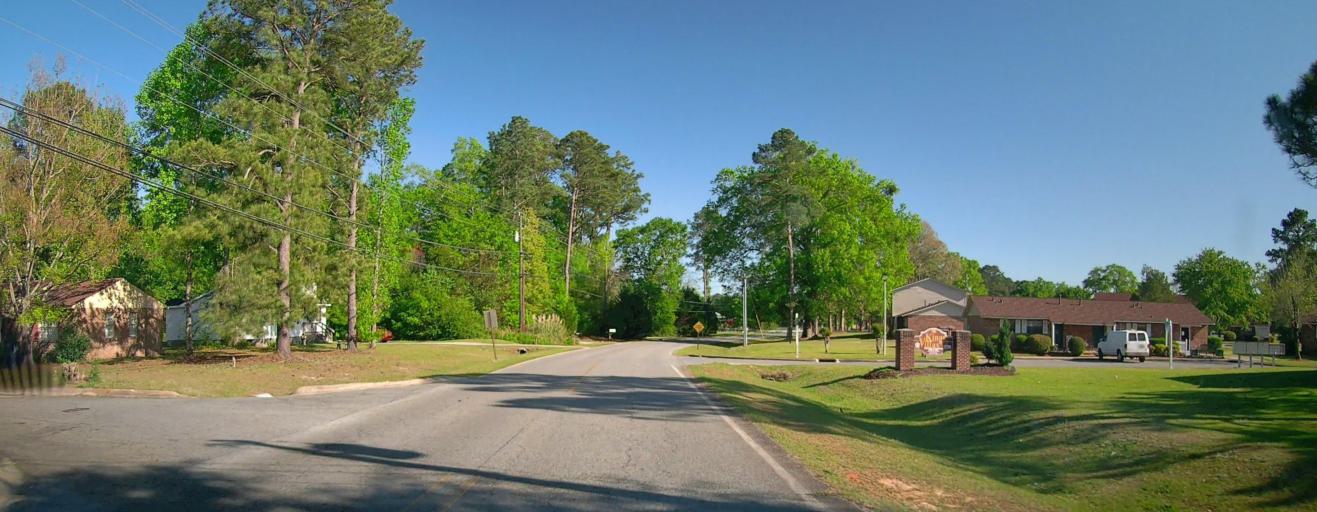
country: US
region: Georgia
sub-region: Houston County
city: Perry
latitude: 32.4672
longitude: -83.7088
